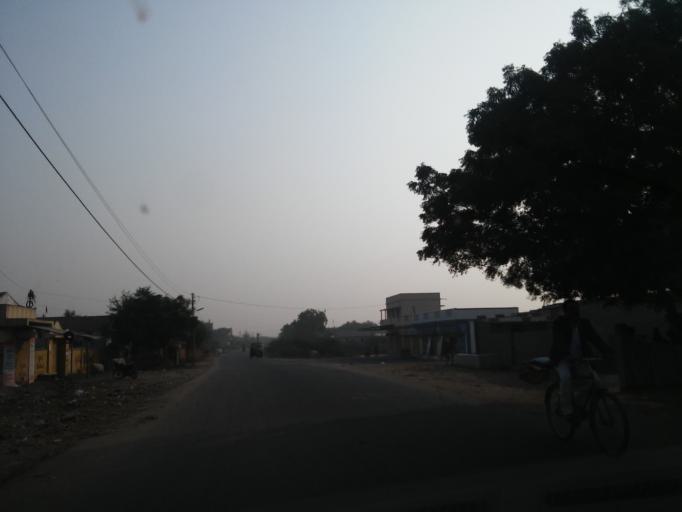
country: IN
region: Gujarat
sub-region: Kachchh
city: Mandvi
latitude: 22.8335
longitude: 69.3656
